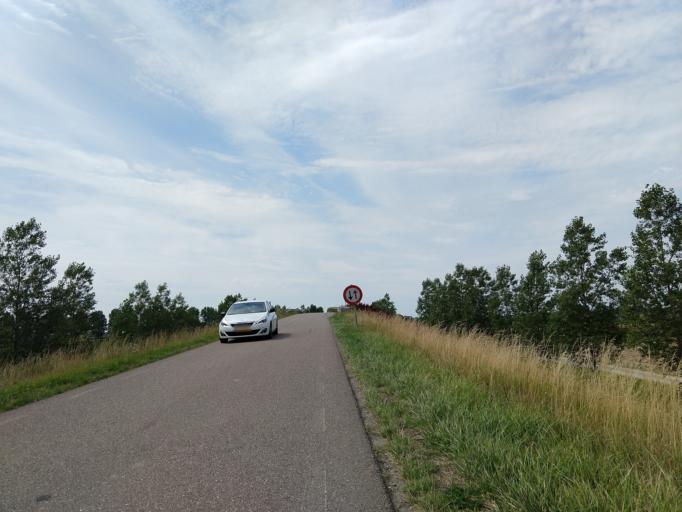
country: NL
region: Zeeland
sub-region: Gemeente Veere
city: Veere
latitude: 51.4902
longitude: 3.7011
